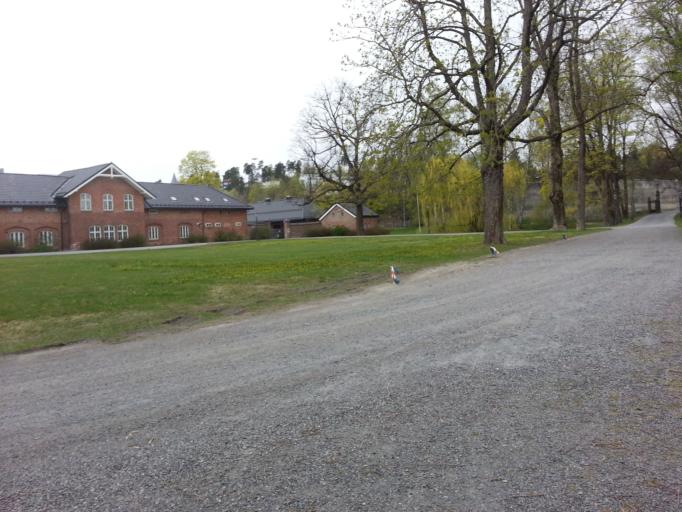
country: NO
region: Akershus
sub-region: Baerum
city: Lysaker
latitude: 59.9145
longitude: 10.6564
